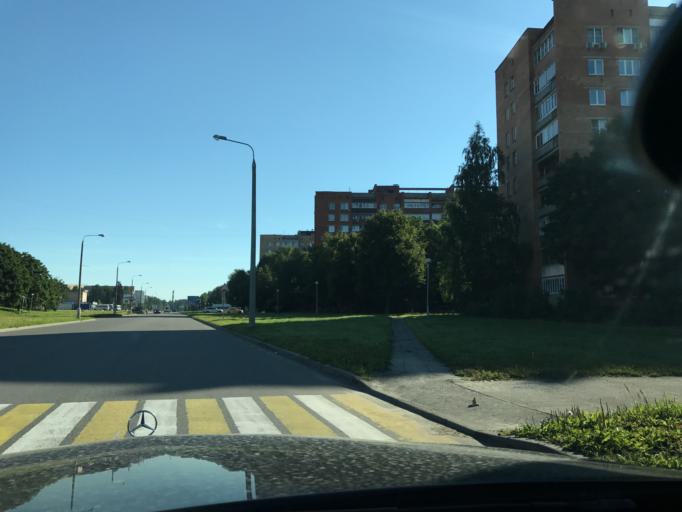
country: RU
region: Moskovskaya
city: Chernogolovka
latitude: 56.0072
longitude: 38.3740
